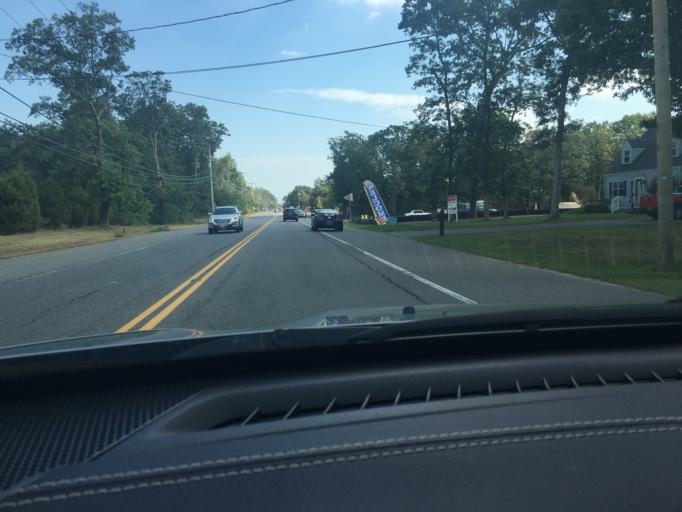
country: US
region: New Jersey
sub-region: Ocean County
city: Leisure Knoll
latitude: 40.0257
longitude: -74.2733
